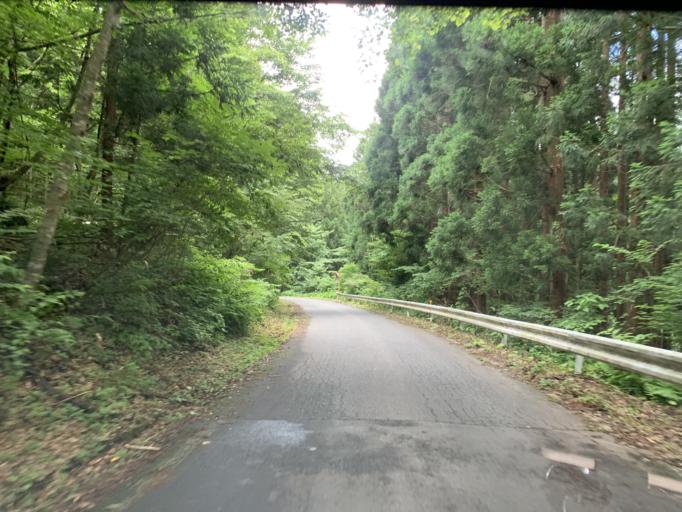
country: JP
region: Iwate
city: Ichinoseki
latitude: 38.9692
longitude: 140.9202
